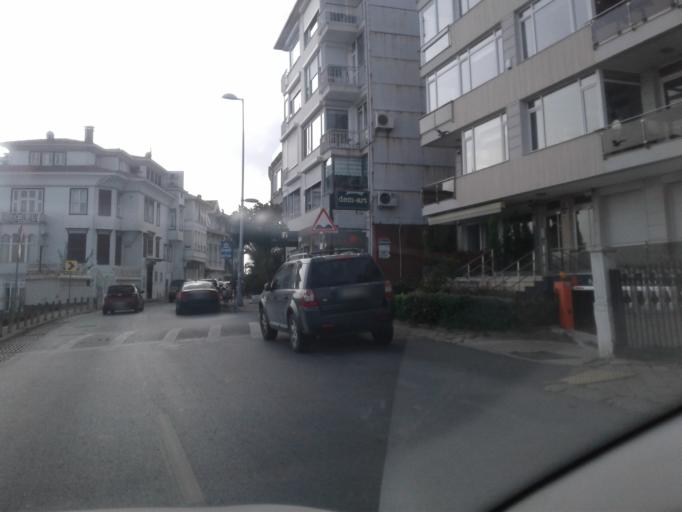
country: TR
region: Istanbul
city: UEskuedar
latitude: 41.0637
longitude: 29.0407
